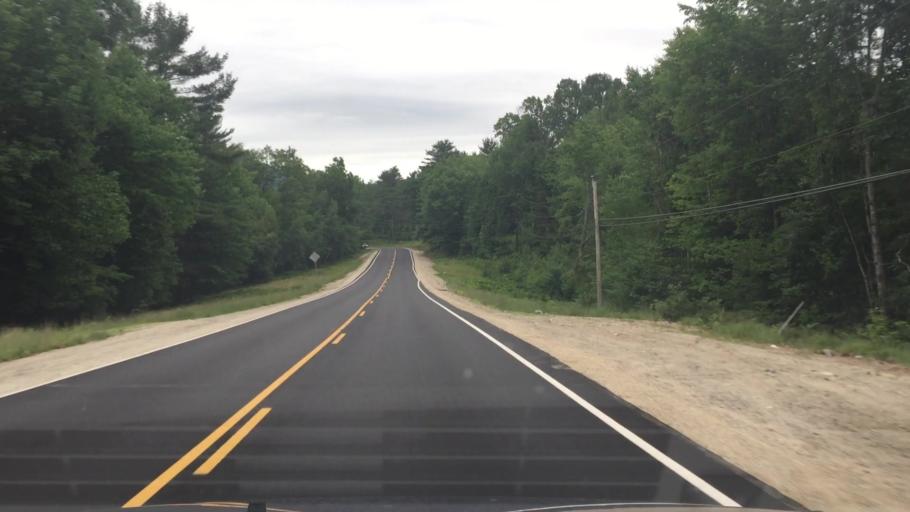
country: US
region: New Hampshire
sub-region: Carroll County
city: Freedom
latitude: 43.8115
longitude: -71.0662
